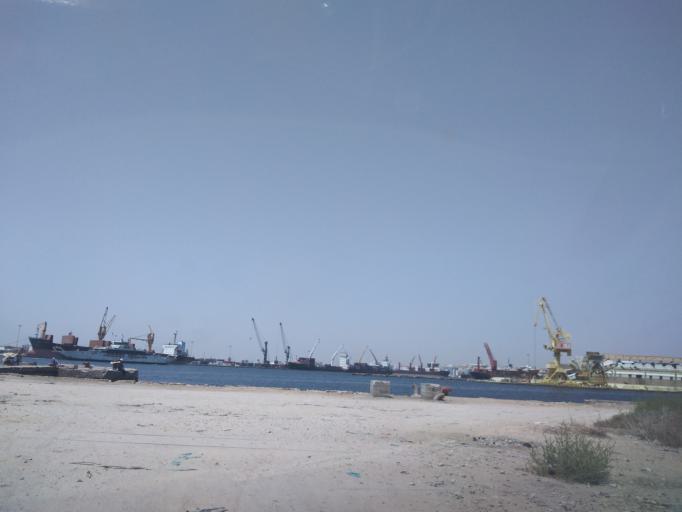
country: TN
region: Safaqis
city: Sfax
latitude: 34.7255
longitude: 10.7795
